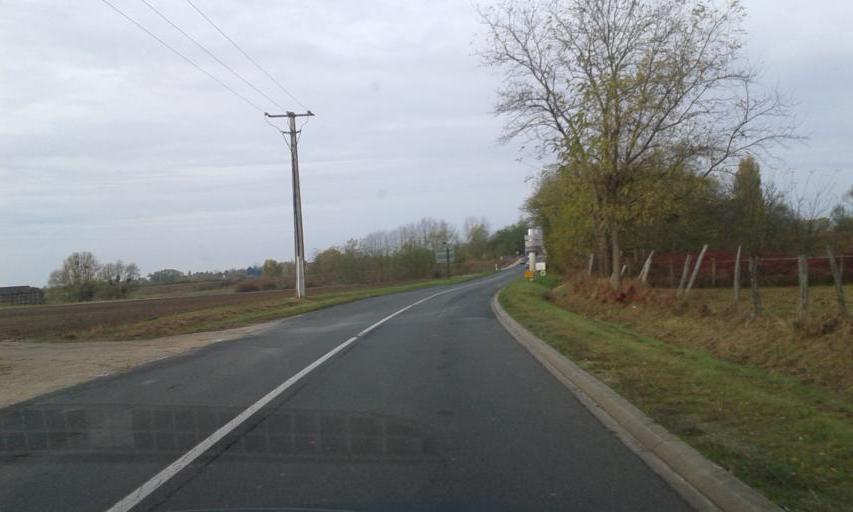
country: FR
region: Centre
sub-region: Departement du Loiret
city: Beaugency
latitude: 47.7758
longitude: 1.6493
